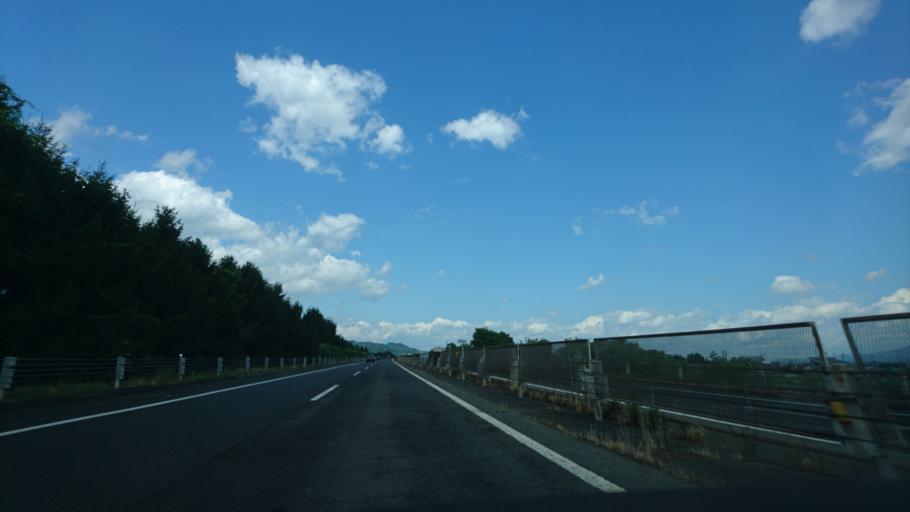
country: JP
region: Iwate
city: Morioka-shi
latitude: 39.7286
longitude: 141.0928
